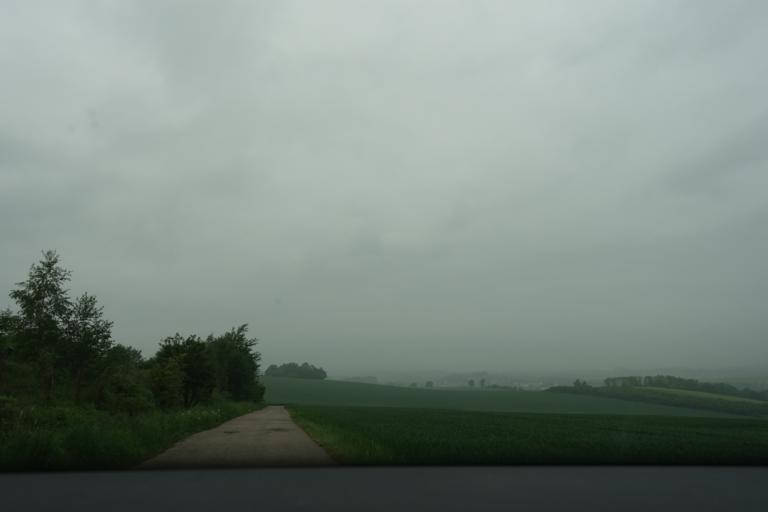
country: DE
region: Saxony
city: Eppendorf
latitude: 50.7780
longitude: 13.2447
